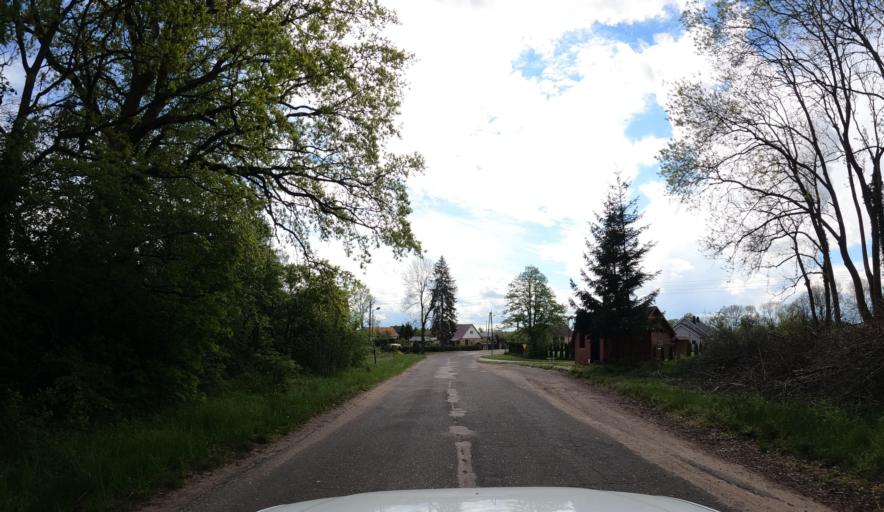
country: PL
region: West Pomeranian Voivodeship
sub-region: Powiat kamienski
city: Wolin
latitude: 53.8684
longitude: 14.6489
